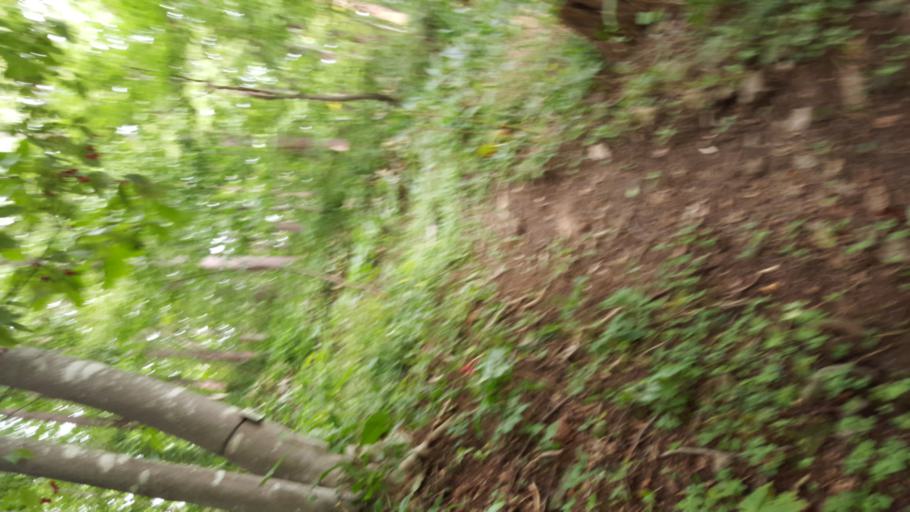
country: JP
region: Hokkaido
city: Otaru
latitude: 43.1319
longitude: 141.1434
